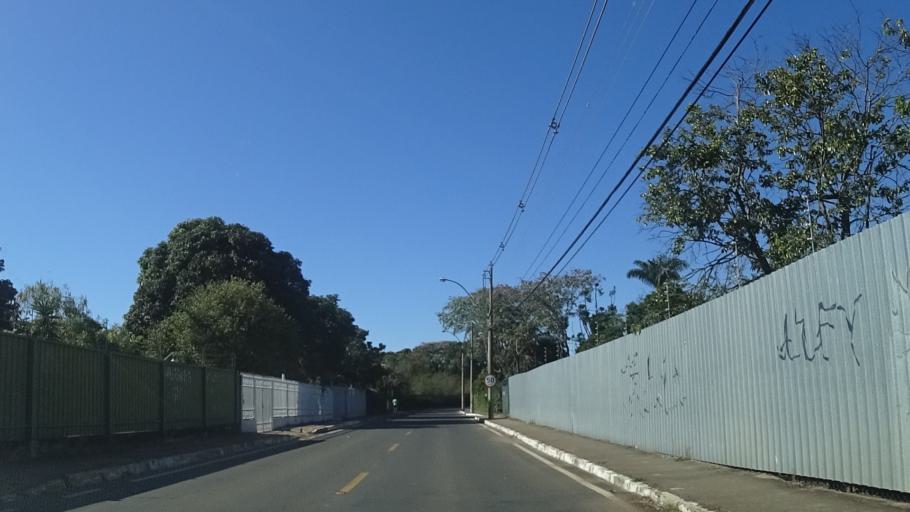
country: BR
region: Federal District
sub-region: Brasilia
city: Brasilia
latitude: -15.7598
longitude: -47.8393
